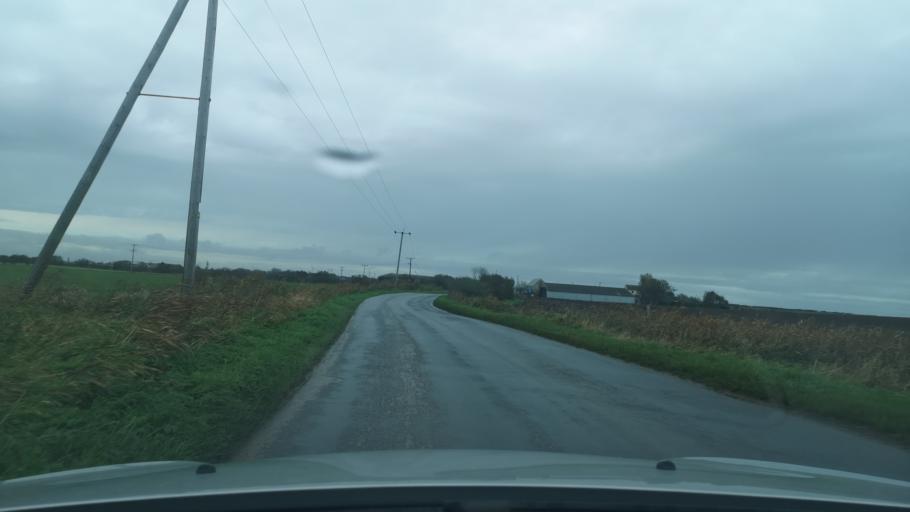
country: GB
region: England
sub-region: East Riding of Yorkshire
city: Easington
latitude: 53.6338
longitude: 0.1218
